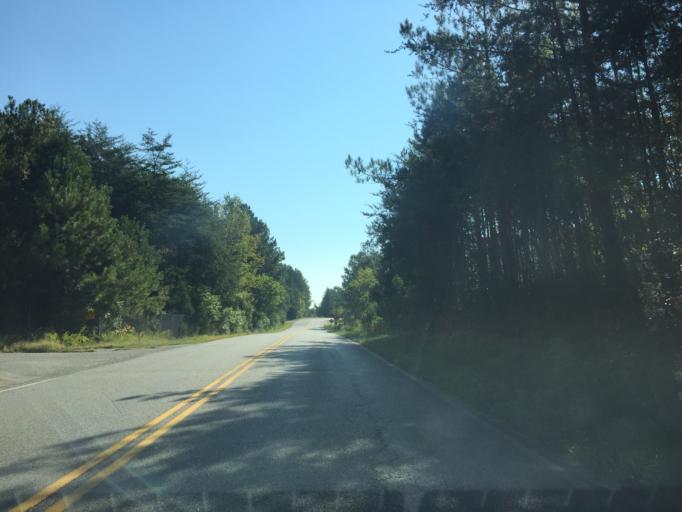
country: US
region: Tennessee
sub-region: Hamilton County
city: Harrison
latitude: 35.0832
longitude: -85.1559
